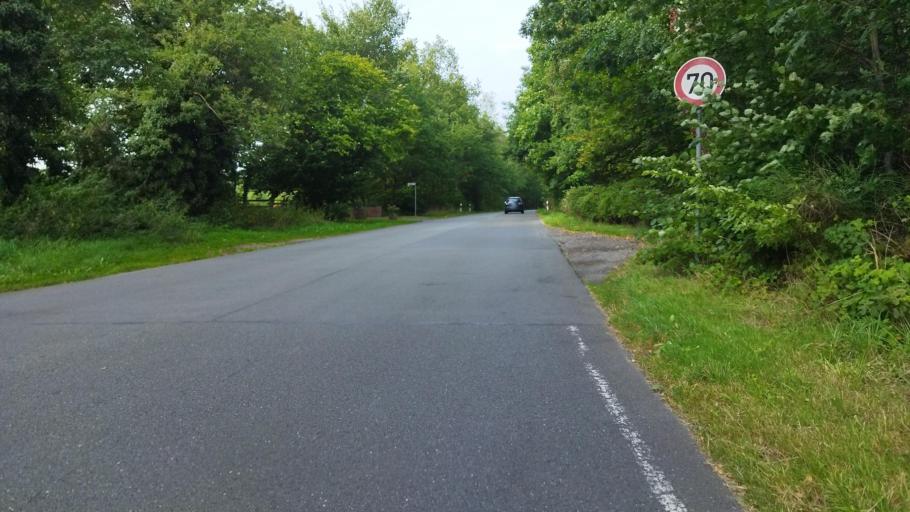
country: DE
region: North Rhine-Westphalia
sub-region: Regierungsbezirk Munster
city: Telgte
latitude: 51.9815
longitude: 7.7363
